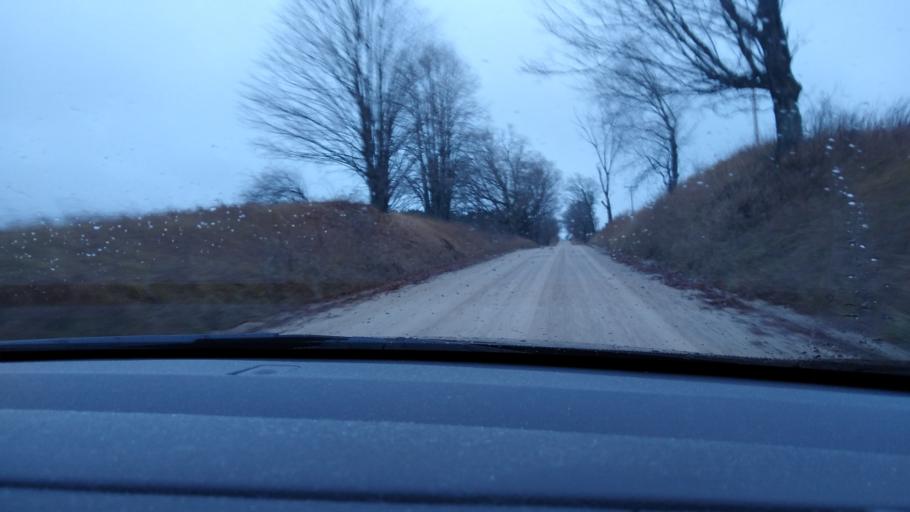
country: US
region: Michigan
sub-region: Wexford County
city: Cadillac
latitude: 44.1715
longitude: -85.3953
